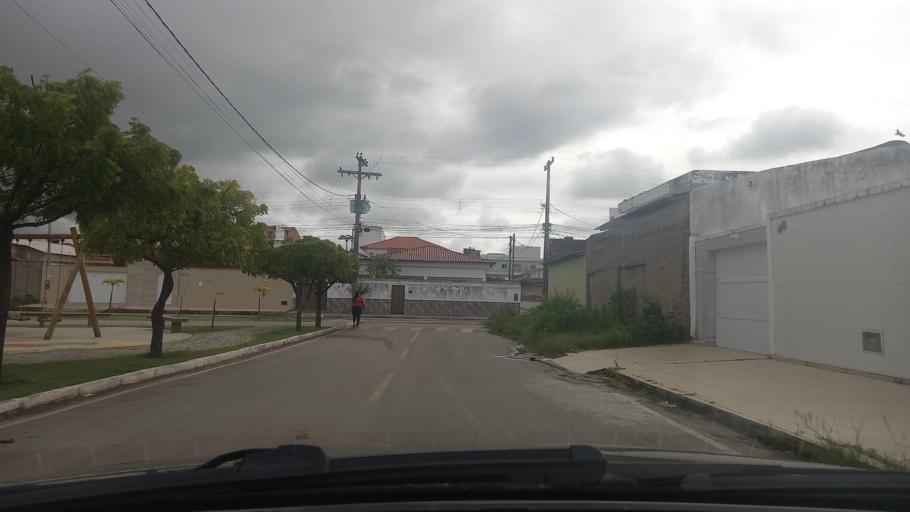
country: BR
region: Bahia
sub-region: Paulo Afonso
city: Paulo Afonso
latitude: -9.4020
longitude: -38.2403
